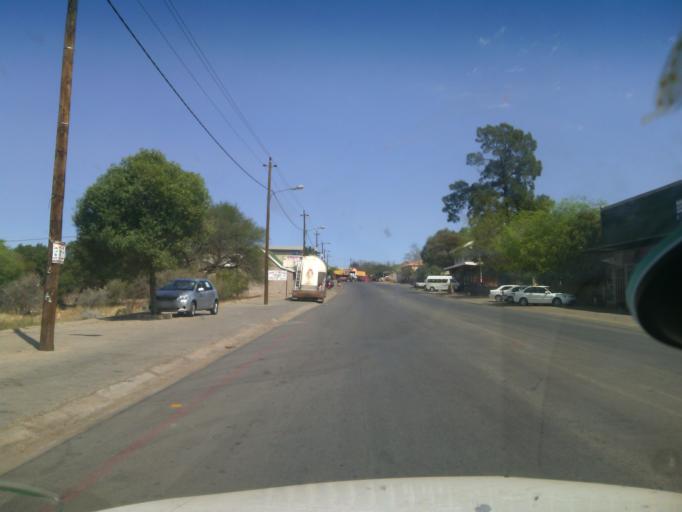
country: ZA
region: Northern Cape
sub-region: Frances Baard District Municipality
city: Barkly West
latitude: -28.5371
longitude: 24.5229
